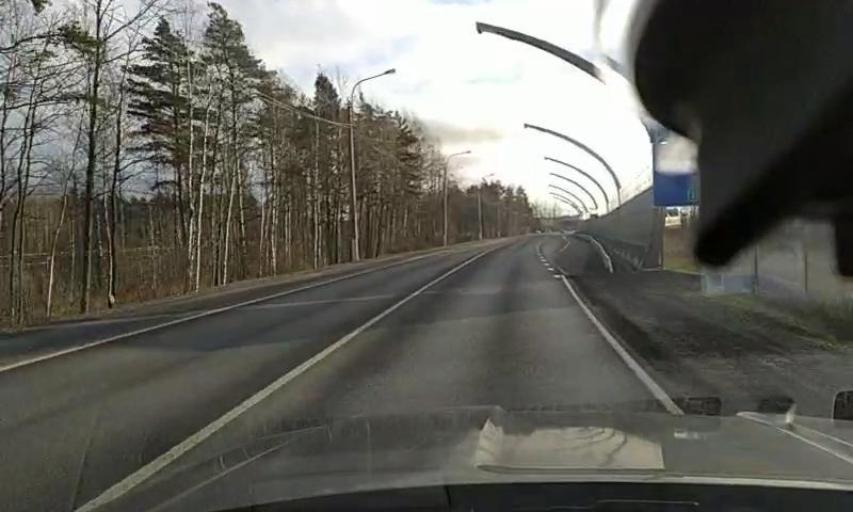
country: RU
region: St.-Petersburg
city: Solnechnoye
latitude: 60.1535
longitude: 29.9656
